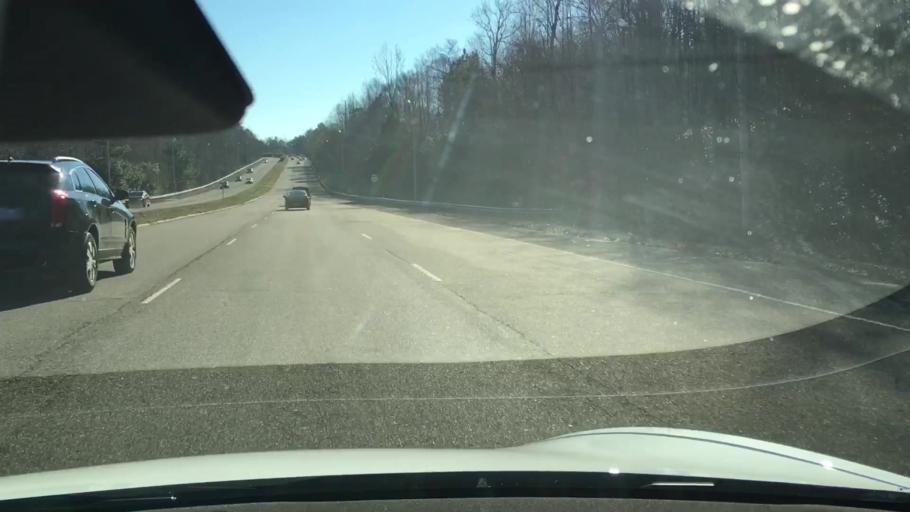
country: US
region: Virginia
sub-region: Chesterfield County
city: Bon Air
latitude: 37.5483
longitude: -77.5634
